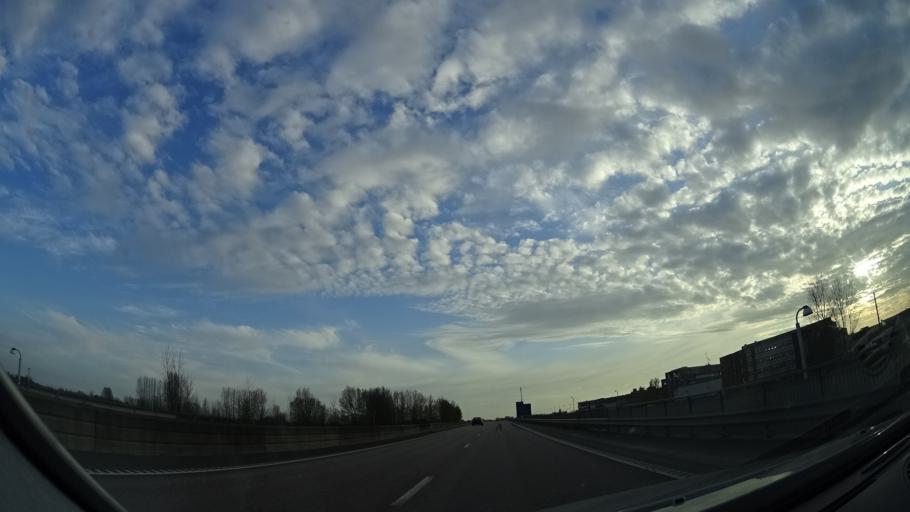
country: SE
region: Skane
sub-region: Lunds Kommun
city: Lund
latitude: 55.6871
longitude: 13.1989
